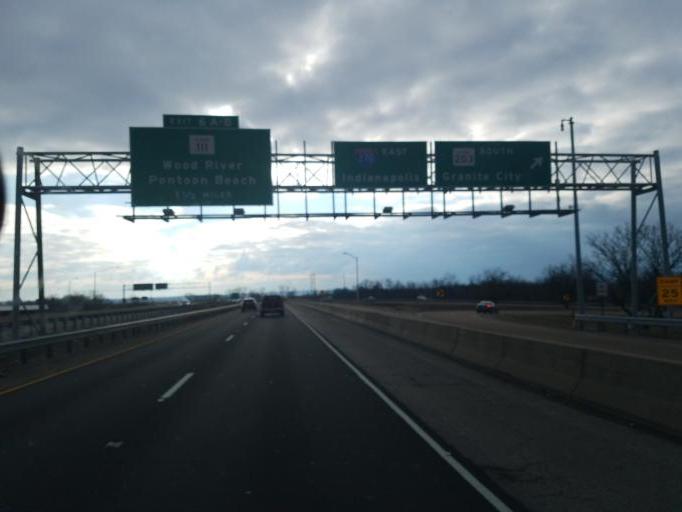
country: US
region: Illinois
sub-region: Madison County
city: Mitchell
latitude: 38.7590
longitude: -90.0933
